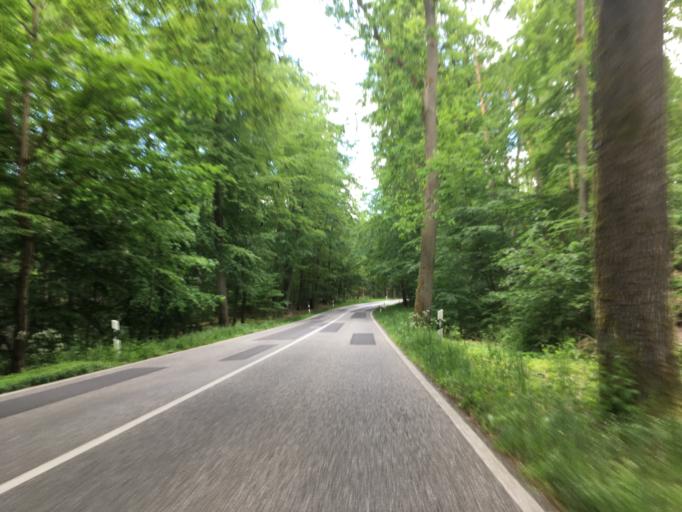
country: DE
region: Brandenburg
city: Bad Freienwalde
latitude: 52.7466
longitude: 13.9850
